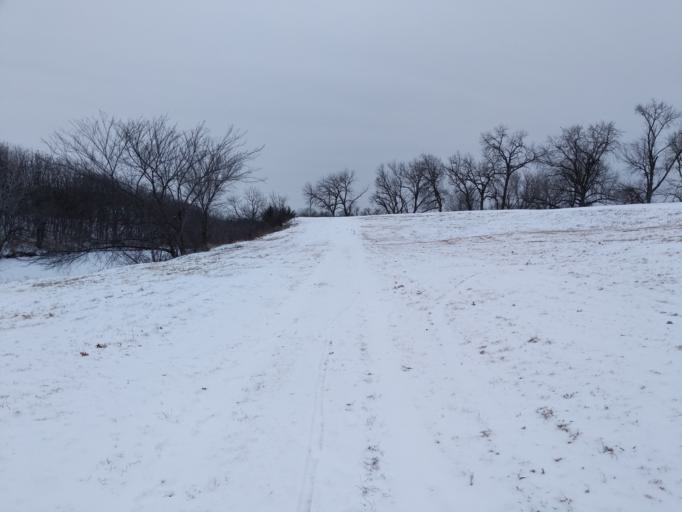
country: US
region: Kansas
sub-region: Morris County
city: Council Grove
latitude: 38.6649
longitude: -96.4913
